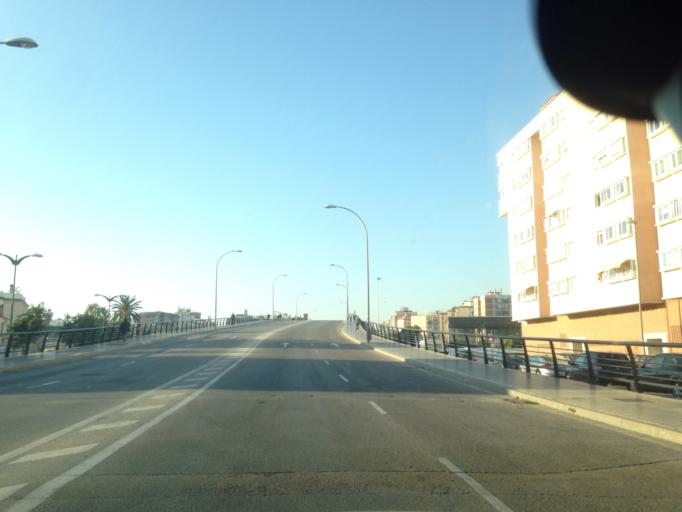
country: ES
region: Andalusia
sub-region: Provincia de Malaga
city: Malaga
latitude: 36.7082
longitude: -4.4355
